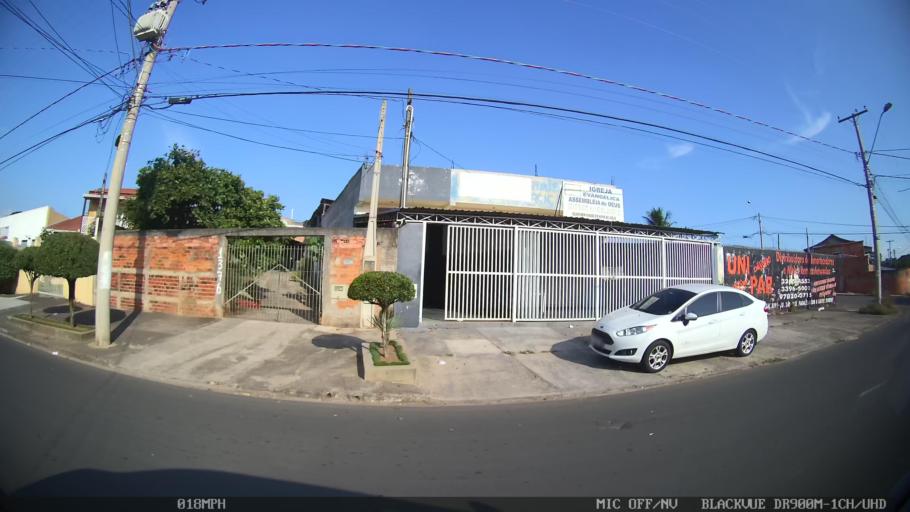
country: BR
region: Sao Paulo
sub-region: Campinas
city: Campinas
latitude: -22.9816
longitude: -47.1421
